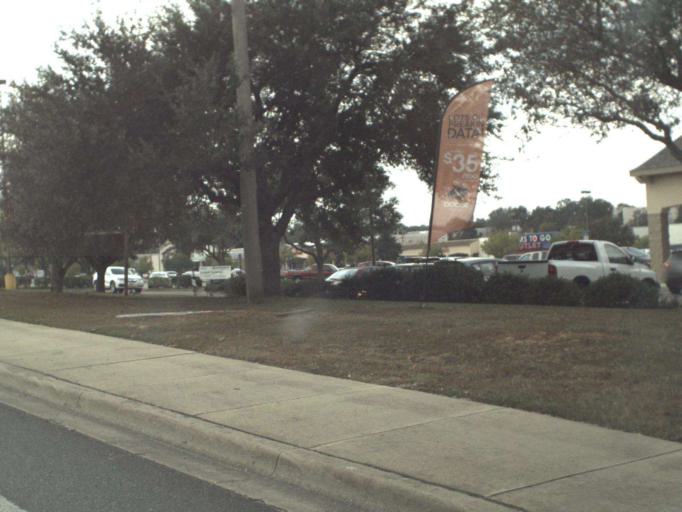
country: US
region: Florida
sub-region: Leon County
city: Tallahassee
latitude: 30.4309
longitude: -84.2268
